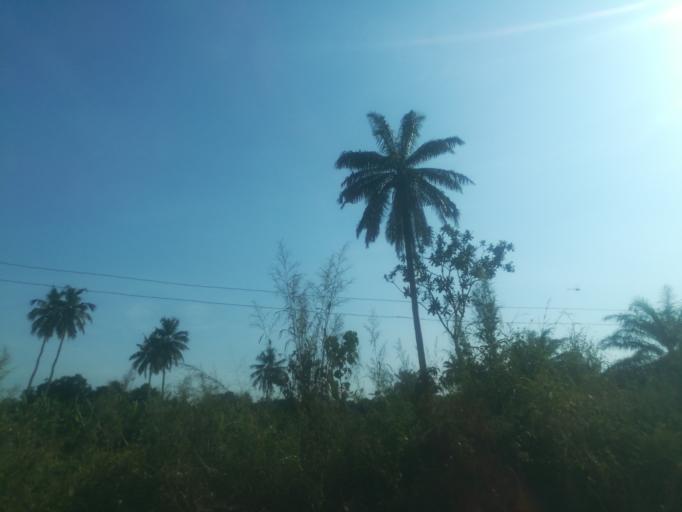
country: NG
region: Ogun
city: Abeokuta
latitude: 7.1401
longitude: 3.2524
